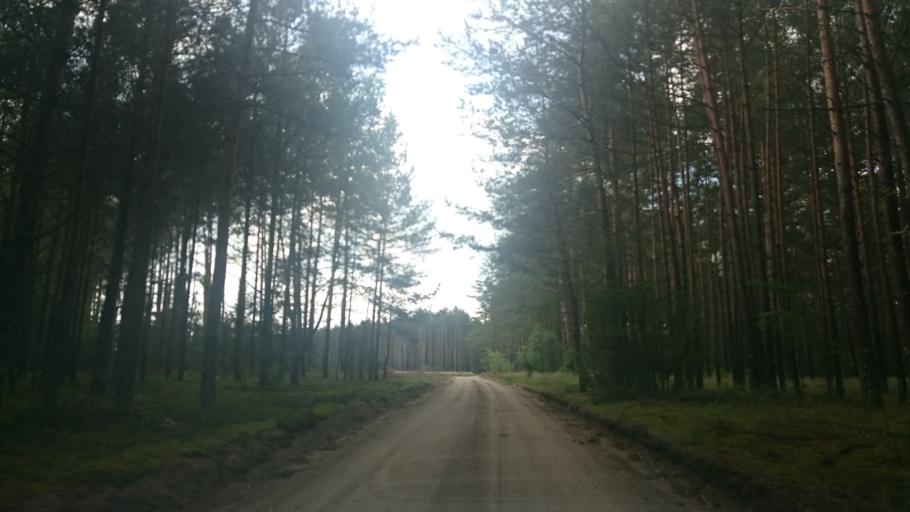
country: PL
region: Pomeranian Voivodeship
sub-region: Powiat koscierski
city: Karsin
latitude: 53.9926
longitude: 17.9340
